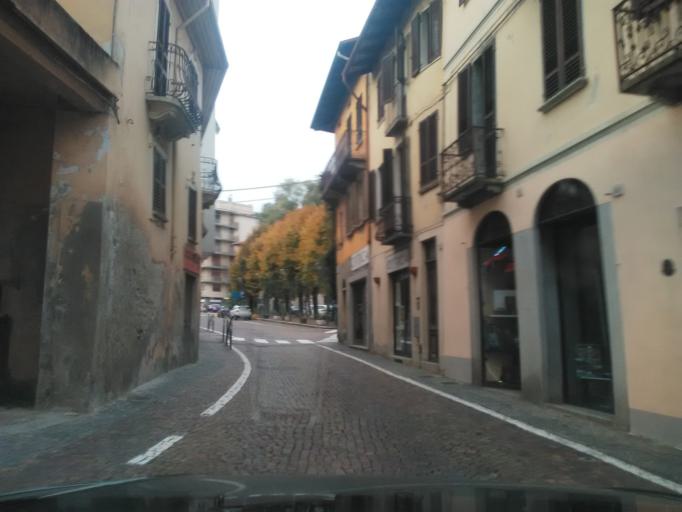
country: IT
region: Piedmont
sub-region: Provincia di Vercelli
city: Borgosesia
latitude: 45.7177
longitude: 8.2756
